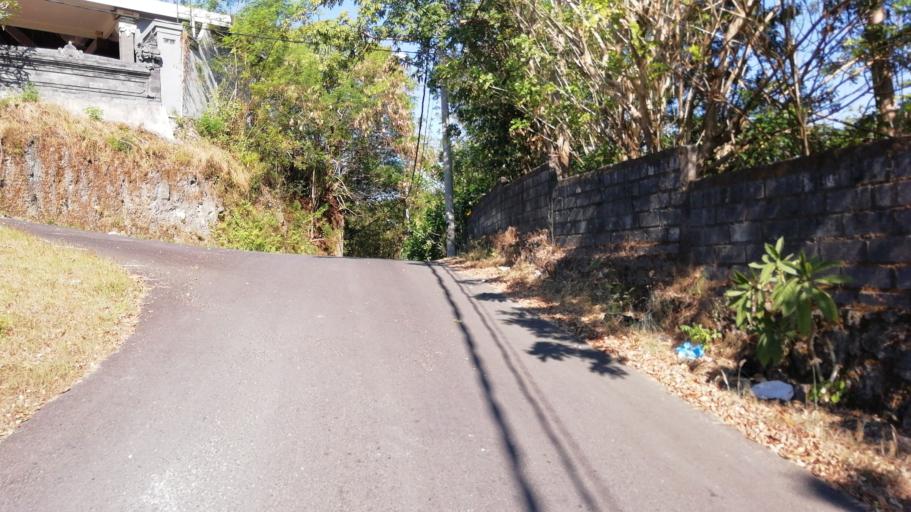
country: ID
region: Bali
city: Jimbaran
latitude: -8.8159
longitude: 115.1619
